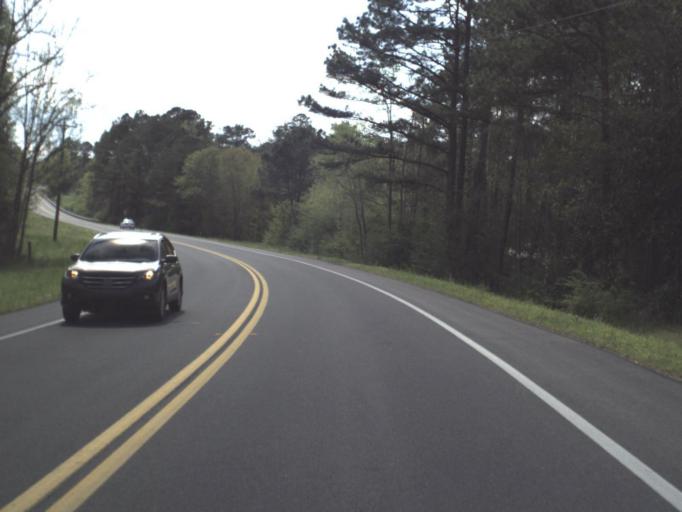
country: US
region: Alabama
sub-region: Covington County
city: Florala
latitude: 30.9655
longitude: -86.4199
